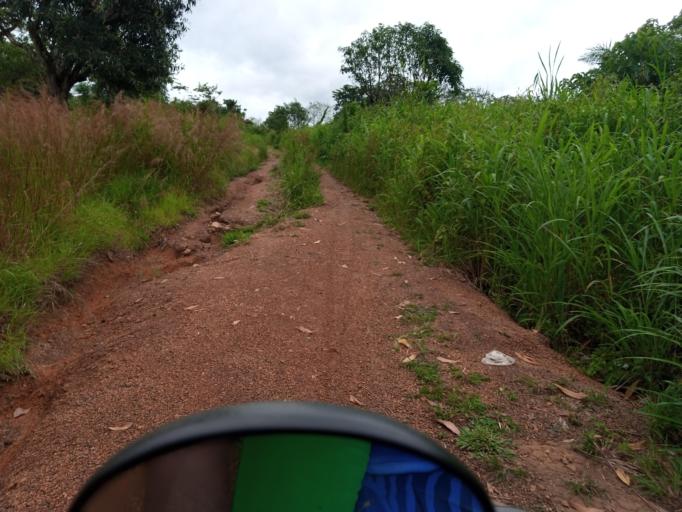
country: SL
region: Southern Province
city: Largo
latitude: 8.1999
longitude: -12.0537
